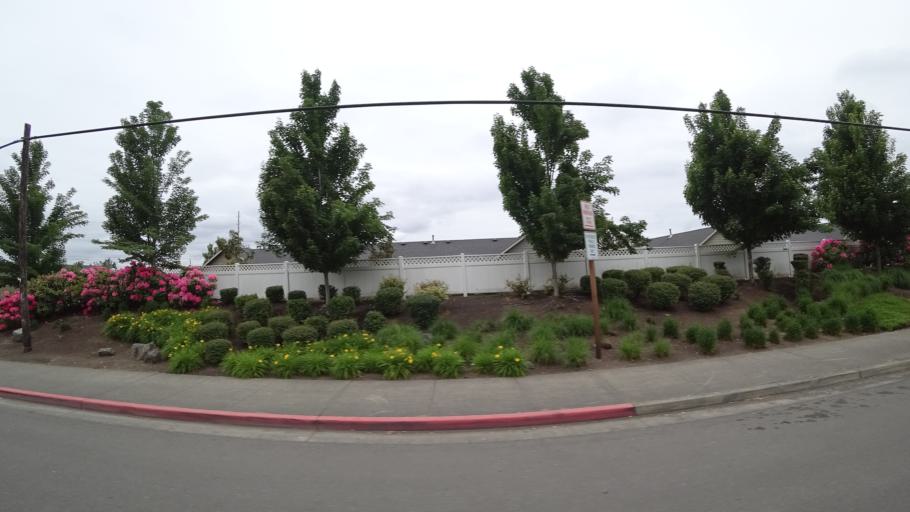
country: US
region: Oregon
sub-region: Multnomah County
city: Fairview
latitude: 45.5425
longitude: -122.4383
